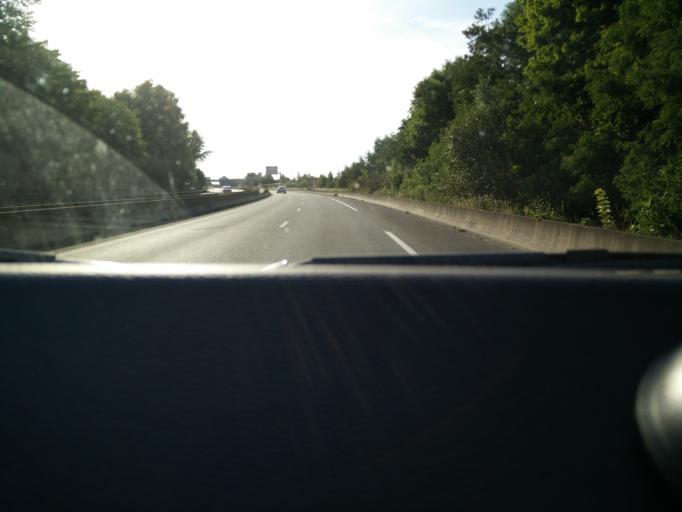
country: FR
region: Nord-Pas-de-Calais
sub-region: Departement du Nord
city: Flers-en-Escrebieux
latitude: 50.4016
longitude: 3.0697
